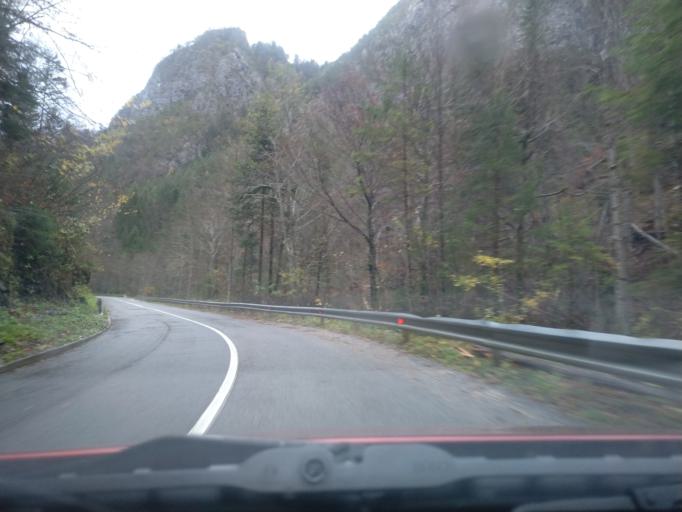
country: SI
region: Solcava
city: Solcava
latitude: 46.4248
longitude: 14.6587
